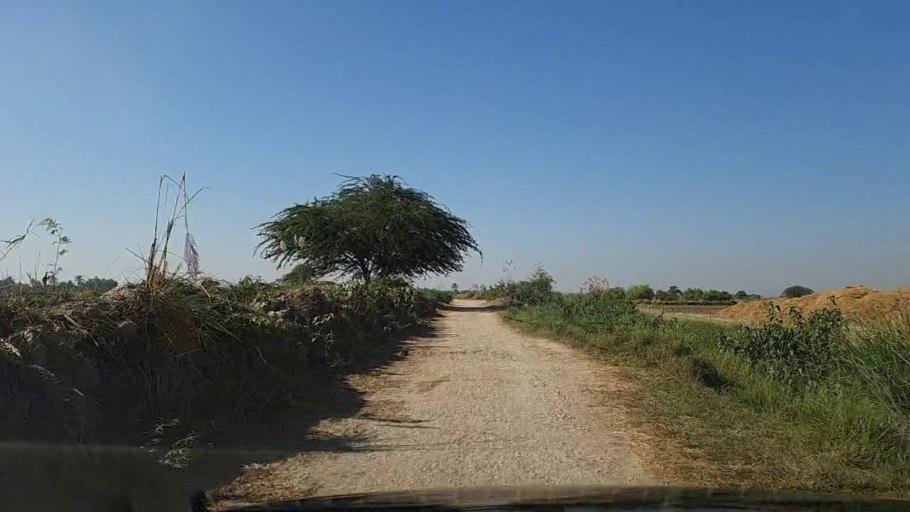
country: PK
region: Sindh
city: Thatta
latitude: 24.7163
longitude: 67.9210
